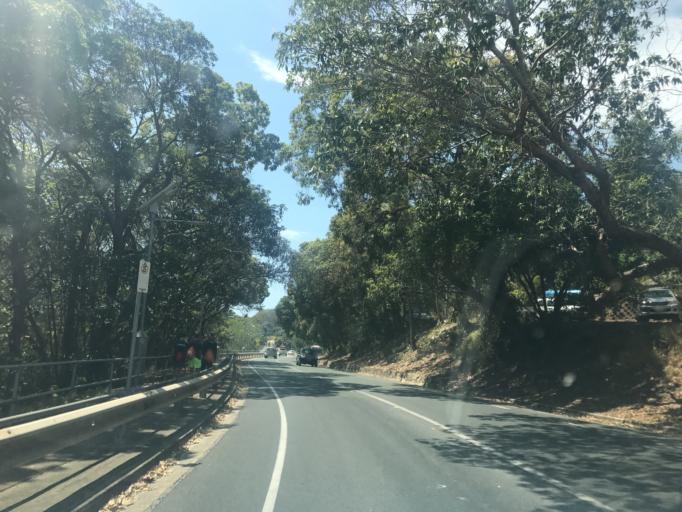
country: AU
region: Queensland
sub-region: Redland
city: Victoria Point
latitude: -27.4277
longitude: 153.5318
